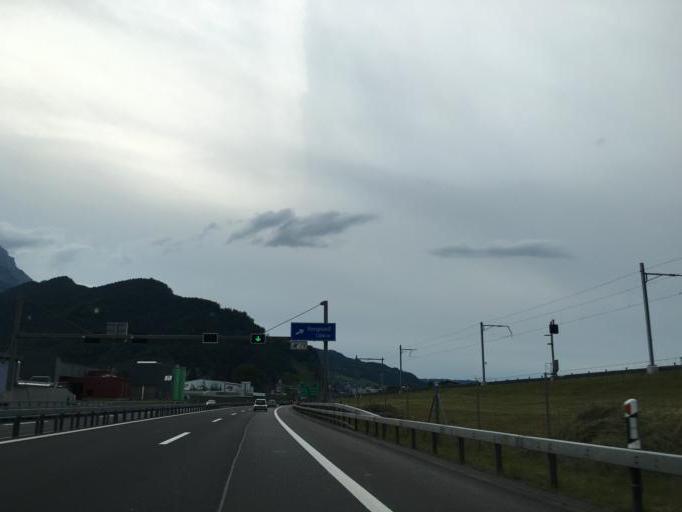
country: CH
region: Nidwalden
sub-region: Nidwalden
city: Stansstad
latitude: 46.9693
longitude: 8.3463
